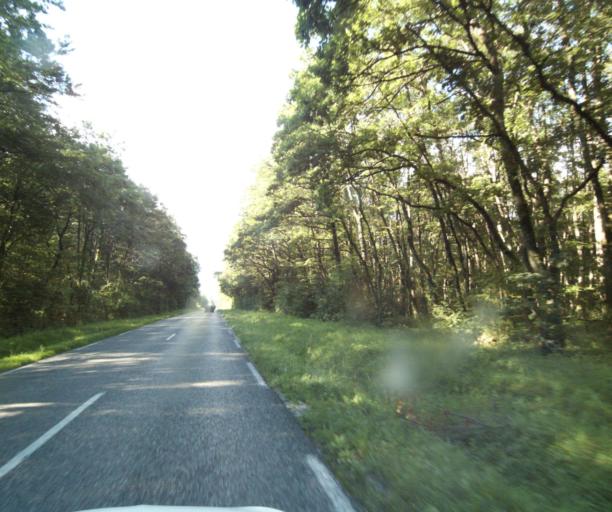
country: FR
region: Rhone-Alpes
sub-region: Departement de la Haute-Savoie
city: Messery
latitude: 46.3374
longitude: 6.2917
